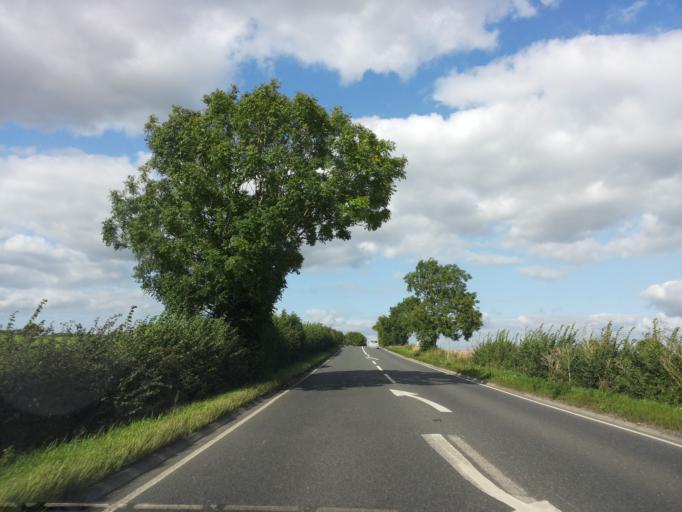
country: GB
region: England
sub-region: Bath and North East Somerset
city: Hinton Charterhouse
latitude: 51.3196
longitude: -2.3099
